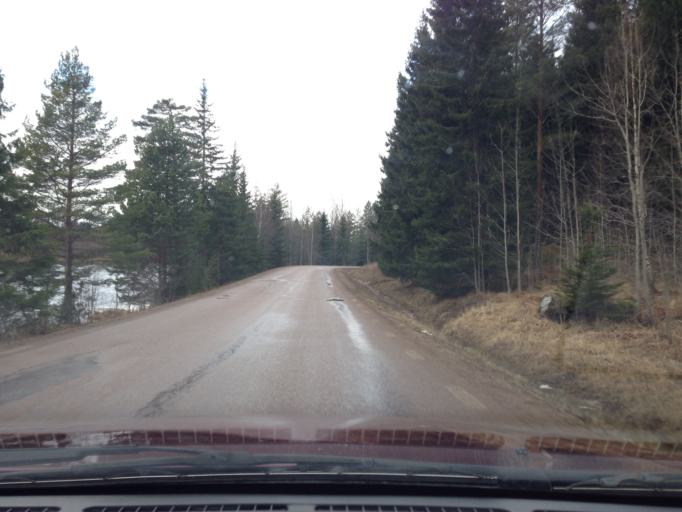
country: SE
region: Dalarna
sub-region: Ludvika Kommun
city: Ludvika
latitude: 60.1592
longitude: 15.2603
